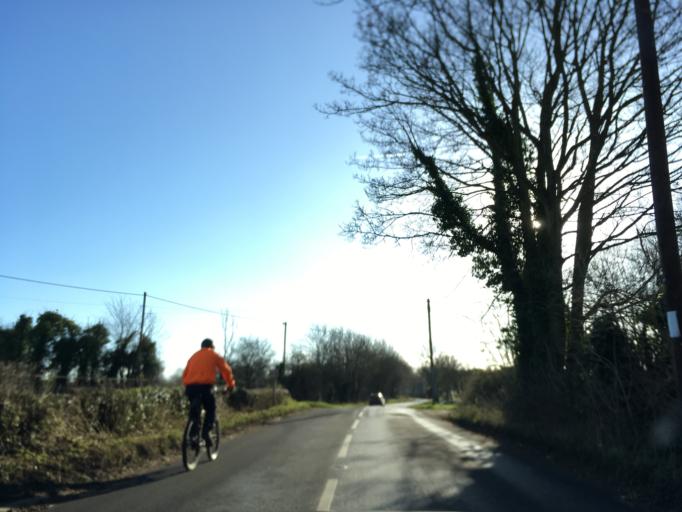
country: GB
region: England
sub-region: Wiltshire
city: Nettleton
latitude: 51.4977
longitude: -2.2216
